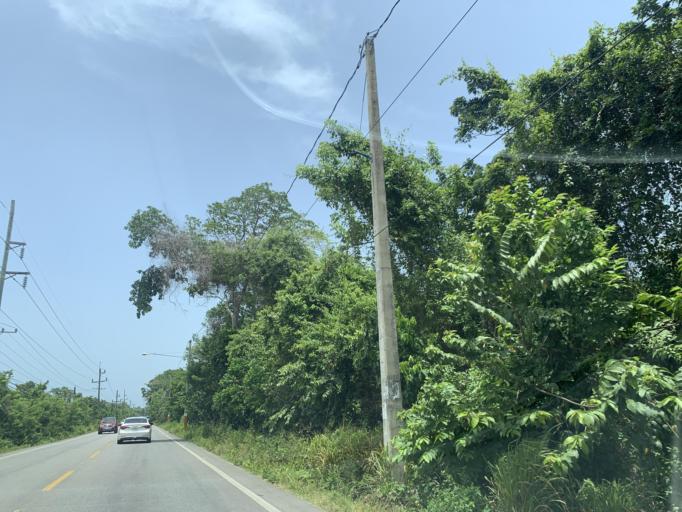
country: DO
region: Puerto Plata
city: Cabarete
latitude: 19.7763
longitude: -70.4692
